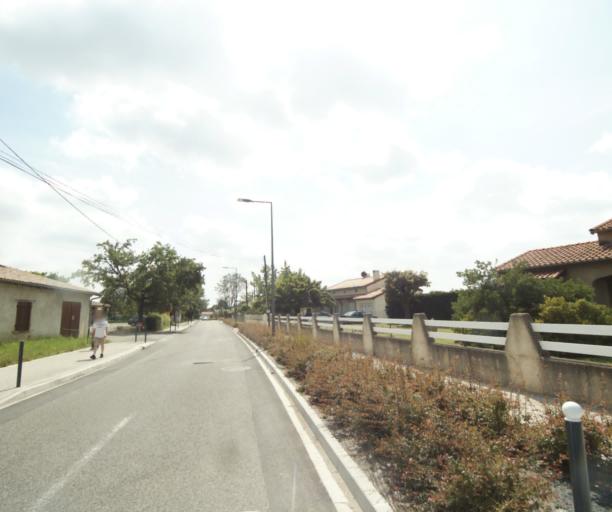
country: FR
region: Midi-Pyrenees
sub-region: Departement du Tarn-et-Garonne
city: Albias
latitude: 44.0614
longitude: 1.4037
